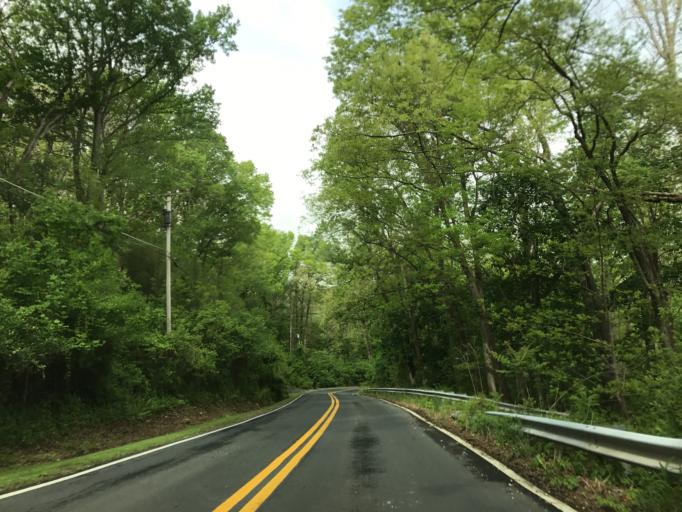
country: US
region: Maryland
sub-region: Carroll County
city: Hampstead
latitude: 39.5367
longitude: -76.8891
